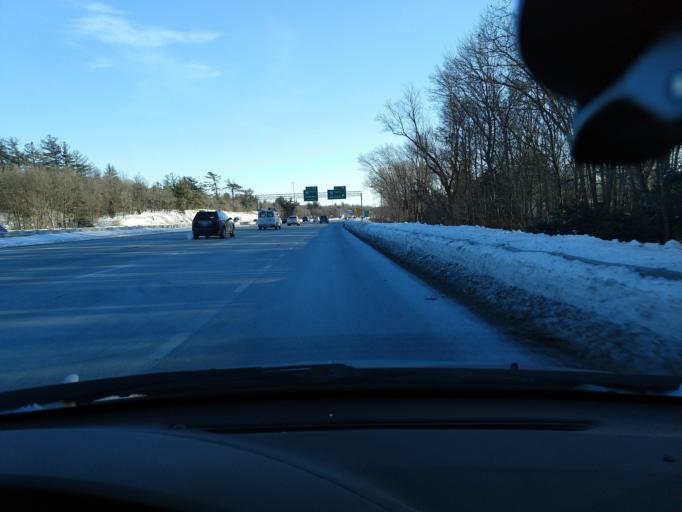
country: US
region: Massachusetts
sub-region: Middlesex County
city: Reading
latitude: 42.5069
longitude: -71.1220
